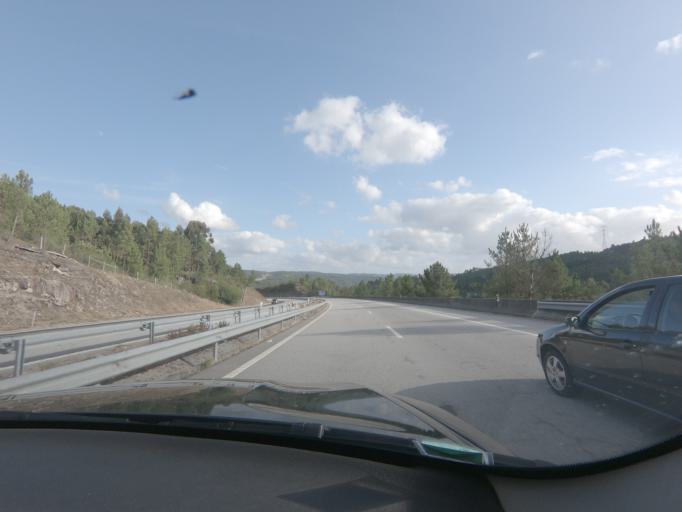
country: PT
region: Viseu
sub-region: Castro Daire
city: Castro Daire
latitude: 40.8118
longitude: -7.9388
